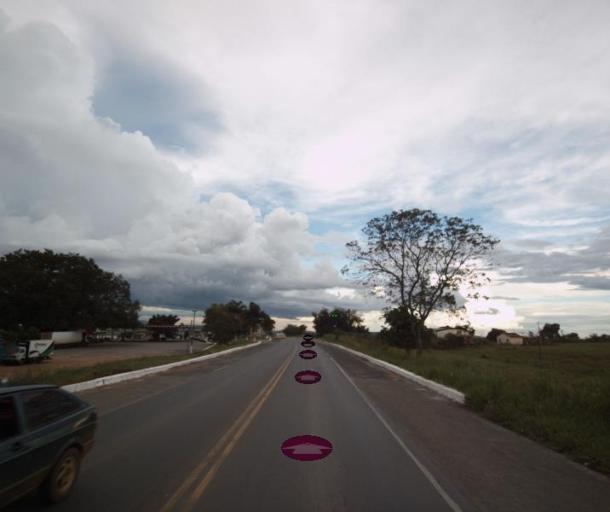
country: BR
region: Goias
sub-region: Itapaci
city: Itapaci
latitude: -14.8564
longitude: -49.3206
